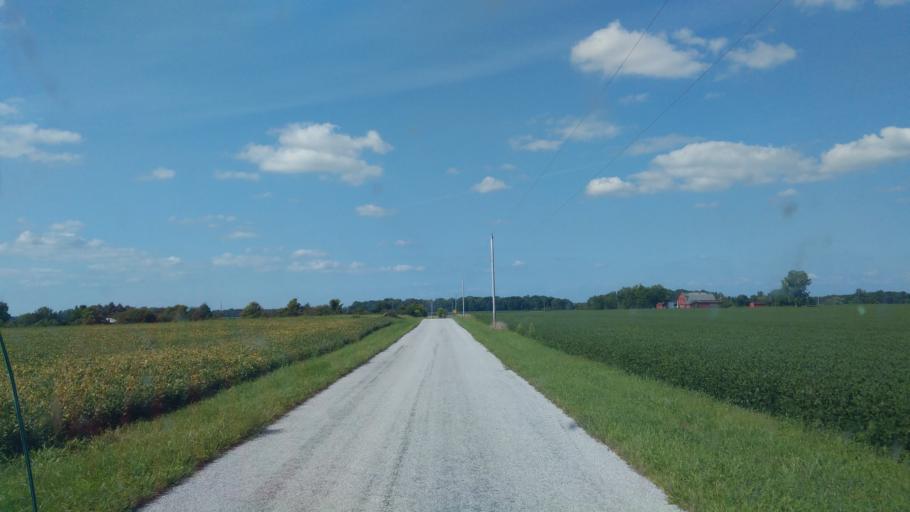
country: US
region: Ohio
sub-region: Hardin County
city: Forest
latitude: 40.6974
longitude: -83.4602
